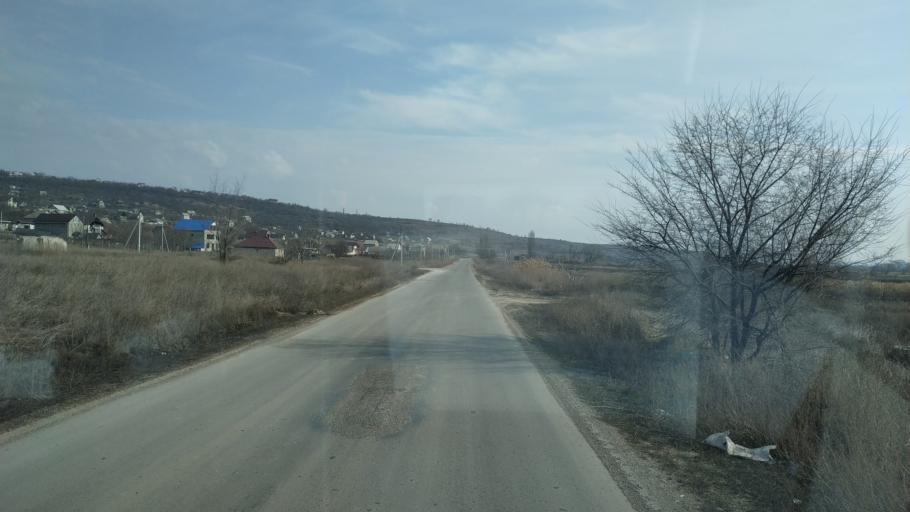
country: MD
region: Chisinau
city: Singera
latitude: 46.9253
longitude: 29.0695
